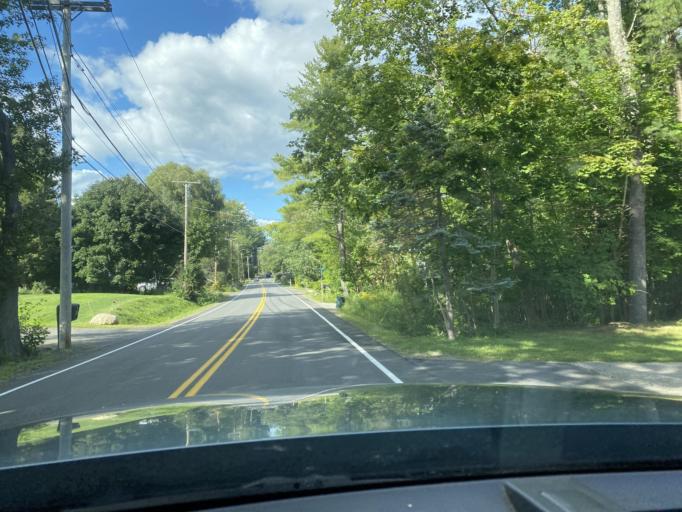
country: US
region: Maine
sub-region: York County
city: Kittery
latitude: 43.1478
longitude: -70.7126
